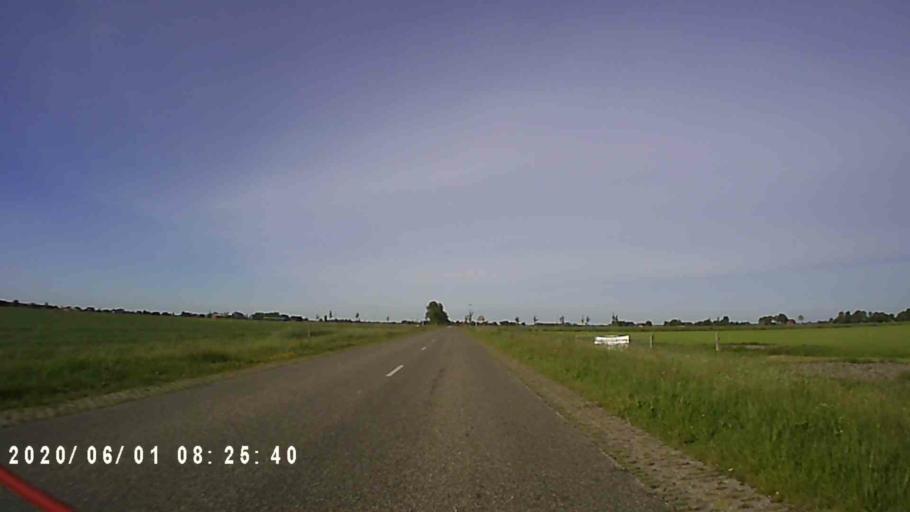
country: NL
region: Friesland
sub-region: Gemeente Ferwerderadiel
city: Burdaard
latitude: 53.2998
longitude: 5.8643
